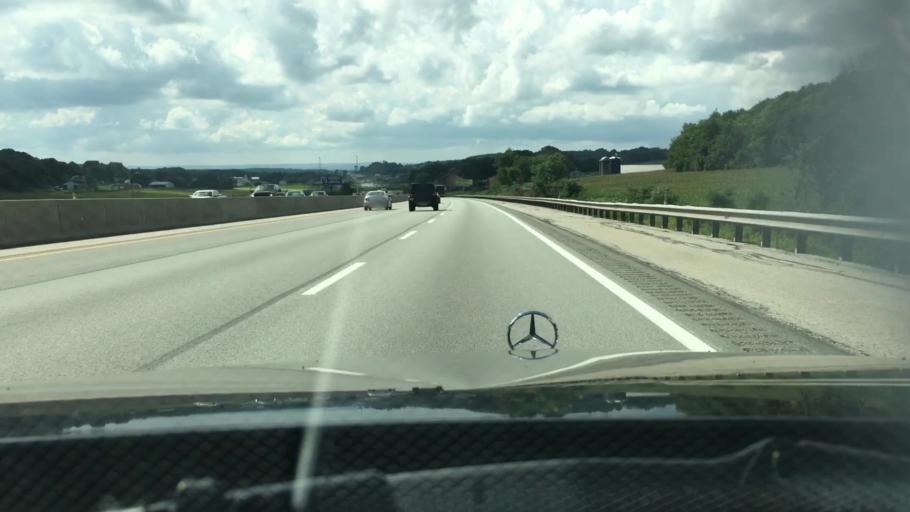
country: US
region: Pennsylvania
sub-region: Somerset County
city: Friedens
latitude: 39.9906
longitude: -78.9847
